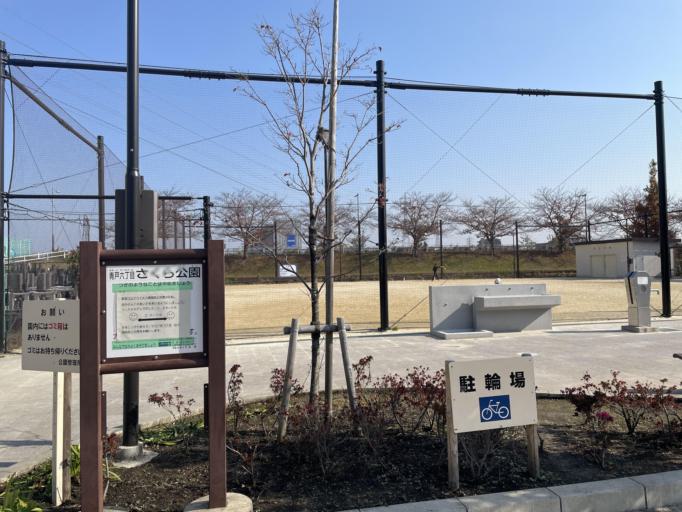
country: JP
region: Chiba
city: Matsudo
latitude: 35.7533
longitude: 139.8577
